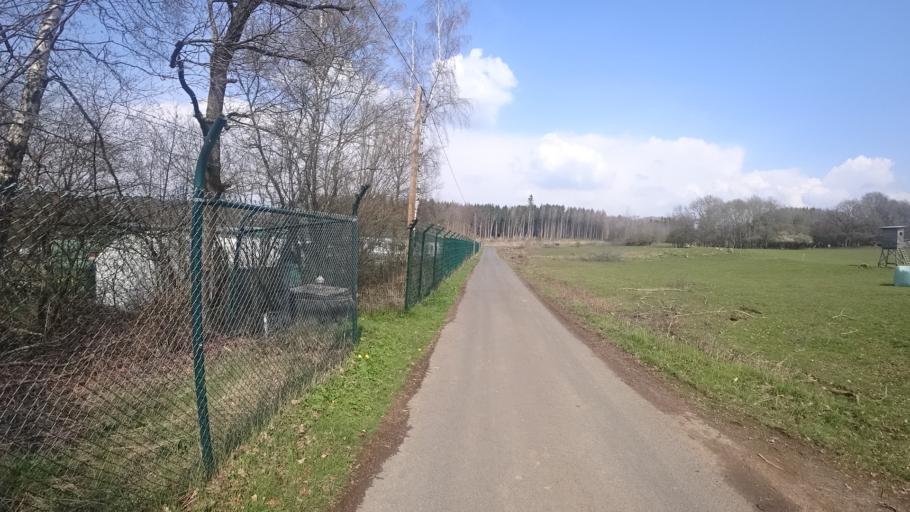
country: DE
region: Rheinland-Pfalz
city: Nauroth
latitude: 50.6936
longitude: 7.8638
